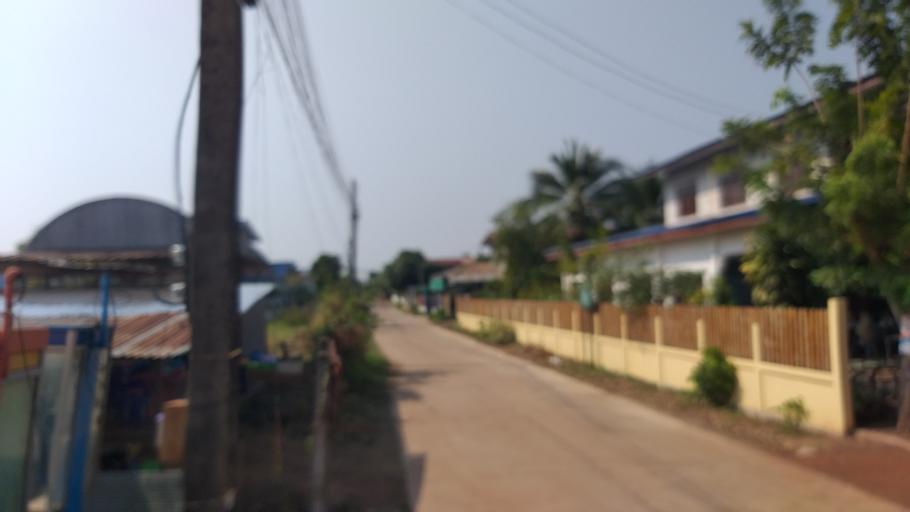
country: TH
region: Changwat Udon Thani
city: Thung Fon
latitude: 17.4553
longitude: 103.1870
